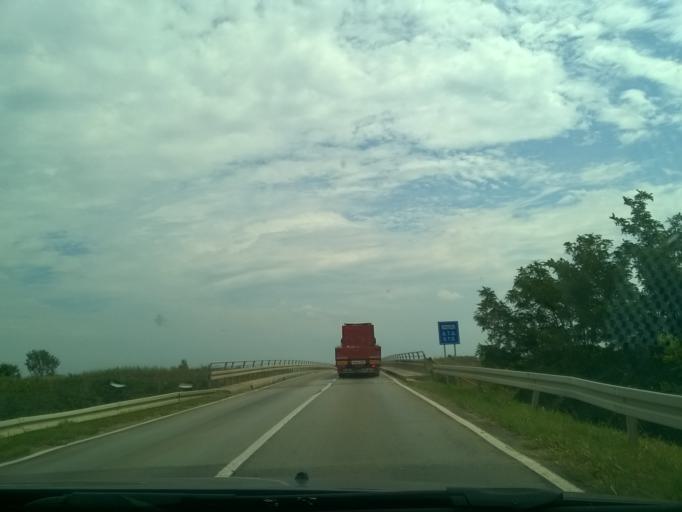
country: RS
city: Klek
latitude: 45.3872
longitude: 20.4941
